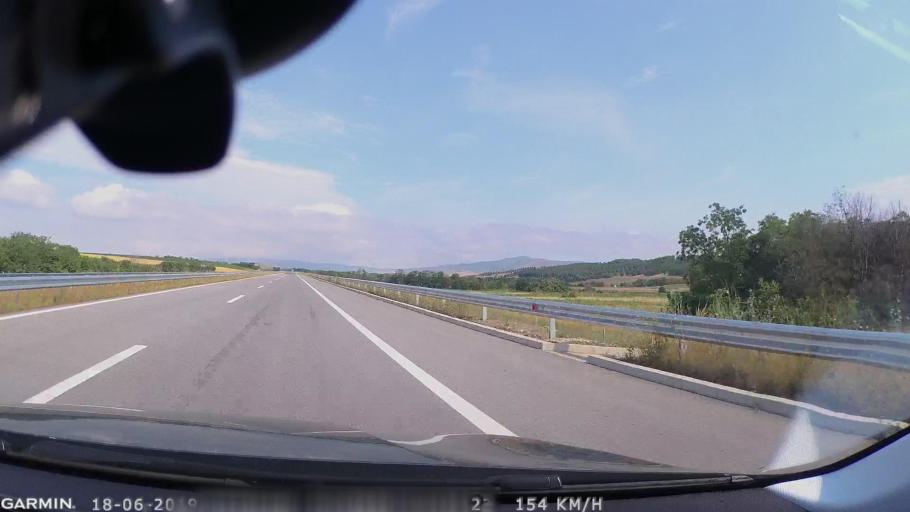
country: MK
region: Sveti Nikole
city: Gorobinci
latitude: 41.9047
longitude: 21.9100
